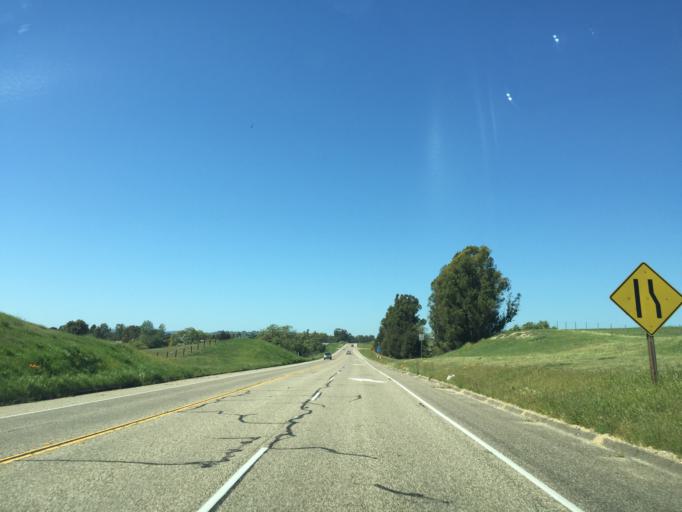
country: US
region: California
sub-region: Santa Barbara County
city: Santa Ynez
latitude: 34.6212
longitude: -120.0677
